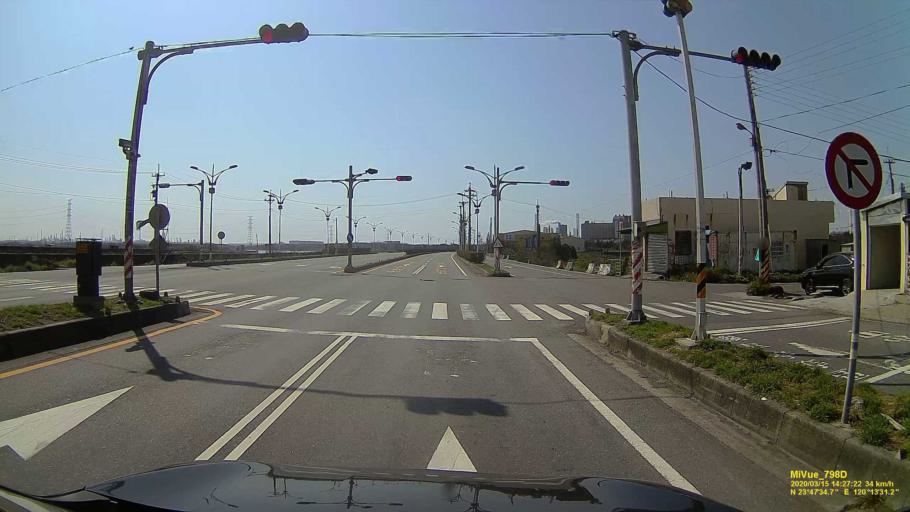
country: TW
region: Taiwan
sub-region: Yunlin
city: Douliu
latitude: 23.7930
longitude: 120.2252
